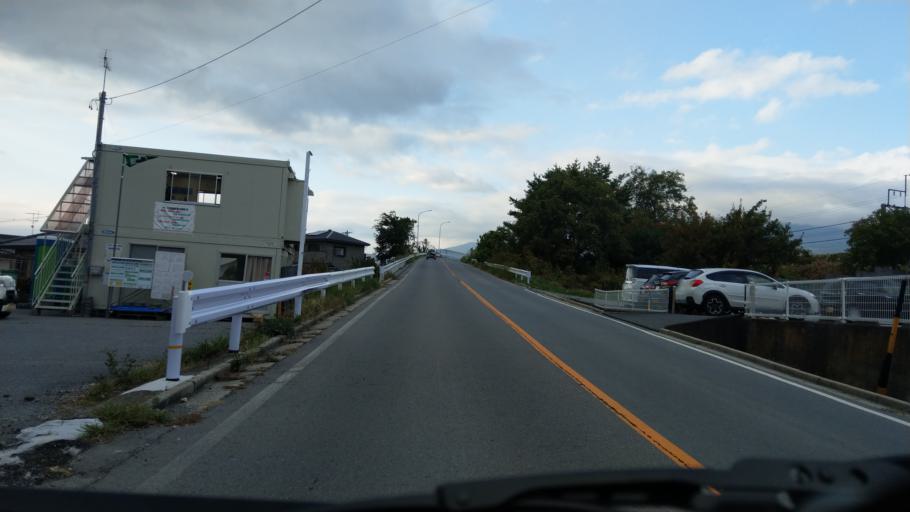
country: JP
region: Nagano
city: Komoro
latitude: 36.3170
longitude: 138.4315
